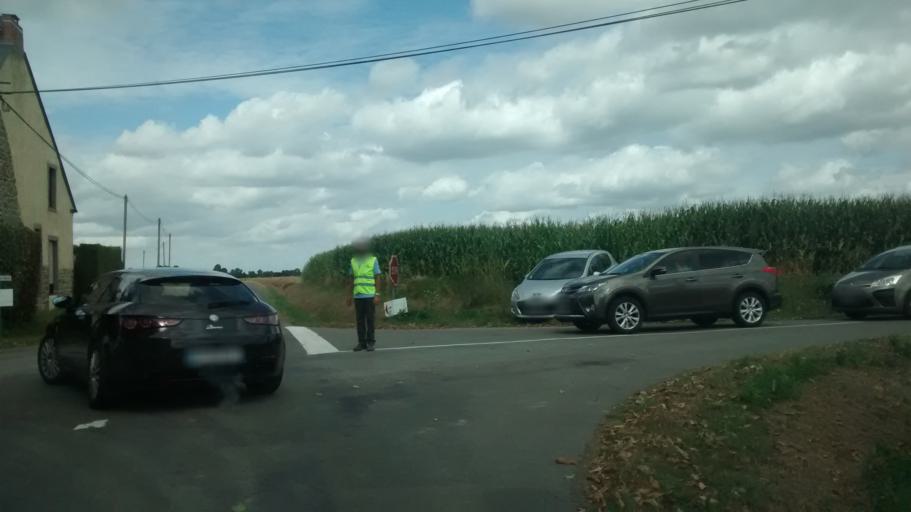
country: FR
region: Brittany
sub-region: Departement d'Ille-et-Vilaine
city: Tinteniac
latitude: 48.3076
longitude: -1.8448
